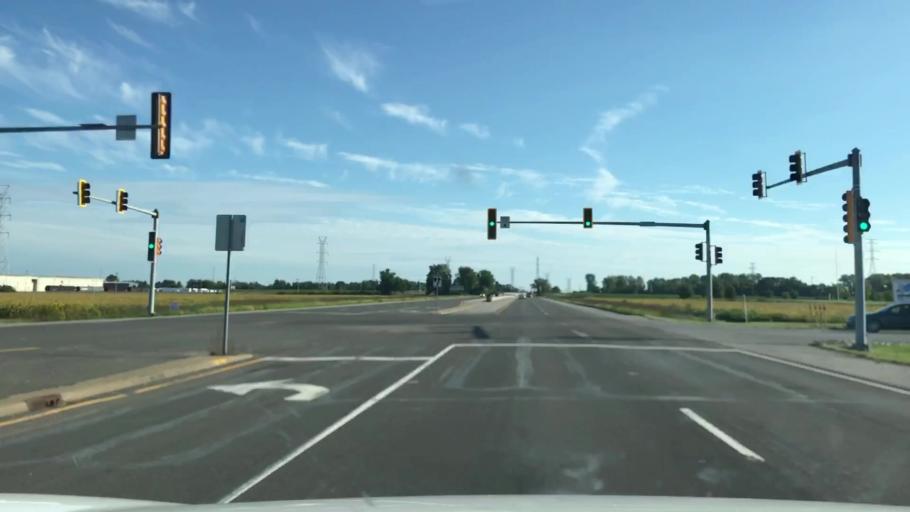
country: US
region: Illinois
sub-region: Madison County
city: Hartford
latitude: 38.8139
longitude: -90.0987
